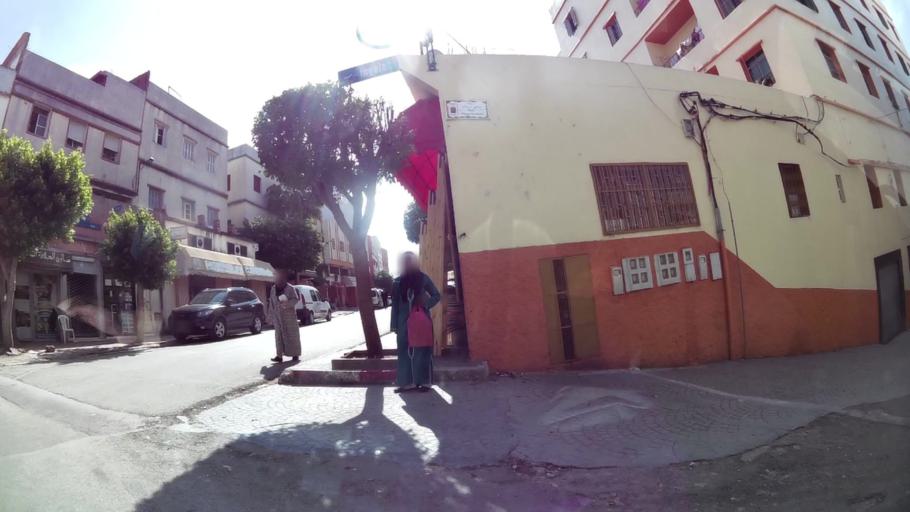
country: MA
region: Tanger-Tetouan
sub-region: Tanger-Assilah
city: Tangier
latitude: 35.7700
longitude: -5.7687
